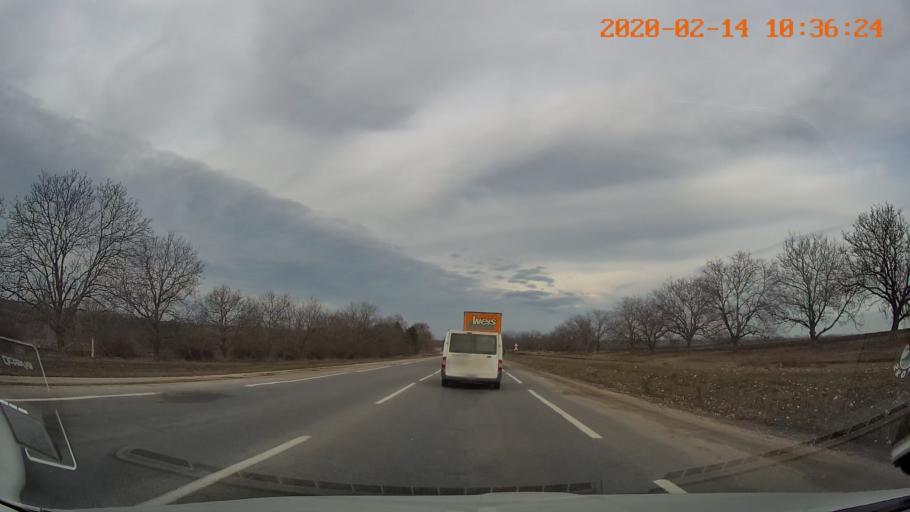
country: MD
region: Riscani
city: Riscani
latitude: 47.9250
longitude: 27.6450
